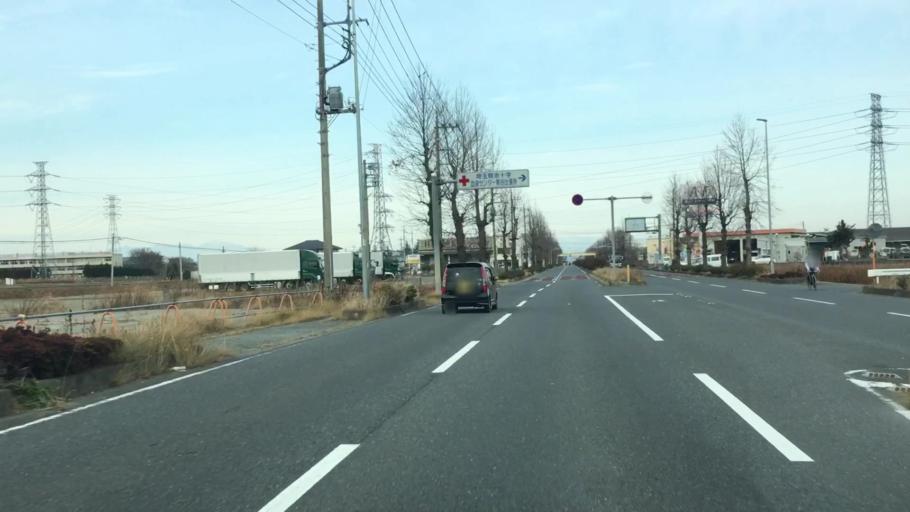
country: JP
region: Saitama
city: Menuma
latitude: 36.1791
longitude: 139.3699
